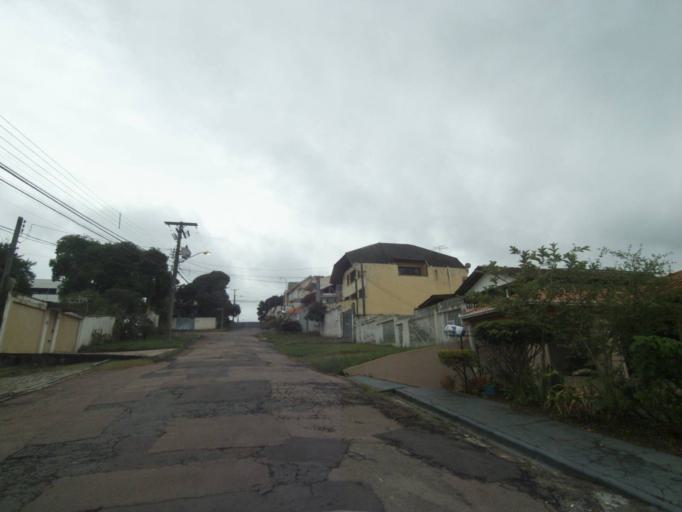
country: BR
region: Parana
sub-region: Curitiba
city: Curitiba
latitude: -25.4273
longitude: -49.3185
